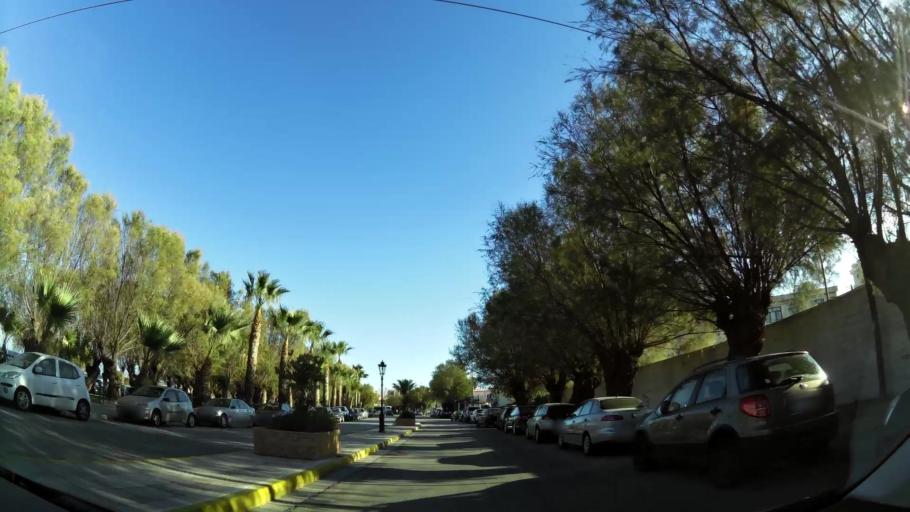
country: GR
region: Attica
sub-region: Nomarchia Anatolikis Attikis
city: Rafina
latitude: 38.0196
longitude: 24.0095
